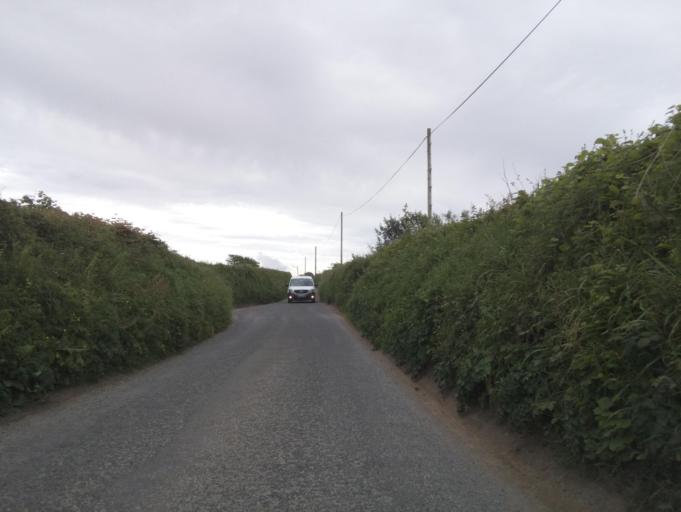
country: GB
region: England
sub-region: Devon
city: Dartmouth
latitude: 50.3199
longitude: -3.6358
